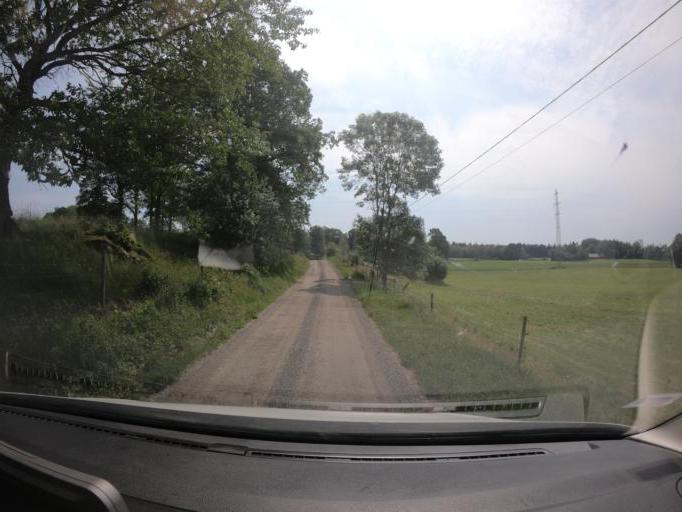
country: SE
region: Skane
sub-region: Hassleholms Kommun
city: Bjarnum
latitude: 56.2669
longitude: 13.6529
